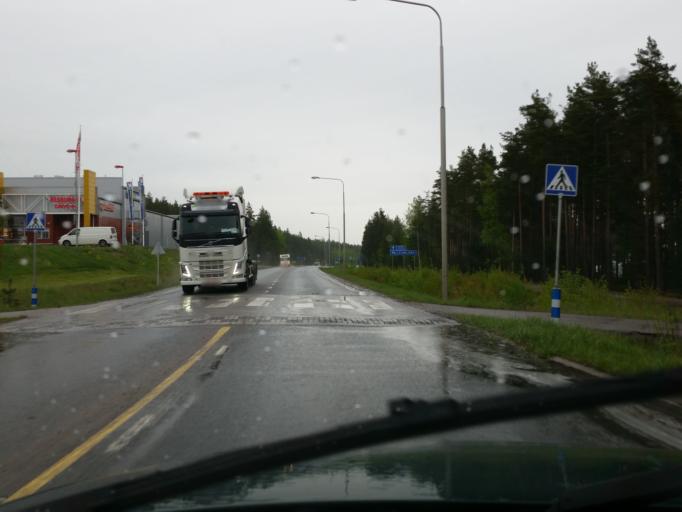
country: FI
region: Uusimaa
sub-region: Helsinki
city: Lohja
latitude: 60.2719
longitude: 24.1225
